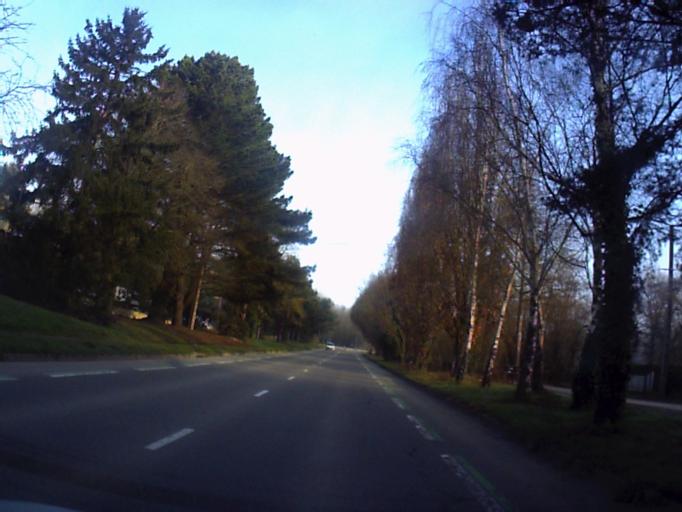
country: FR
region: Brittany
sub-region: Departement d'Ille-et-Vilaine
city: Rennes
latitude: 48.1361
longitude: -1.6522
